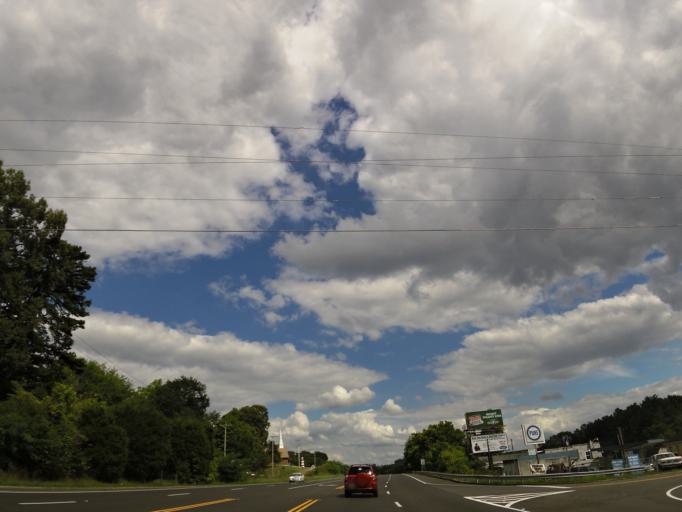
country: US
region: Georgia
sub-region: Walker County
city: Fairview
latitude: 34.9482
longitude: -85.2896
